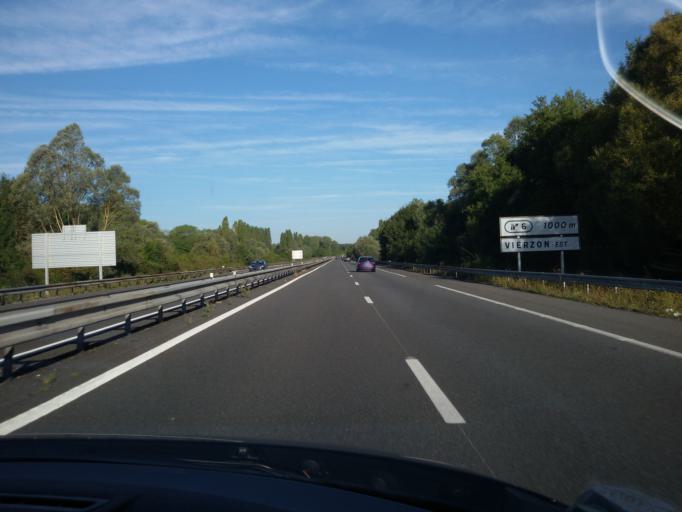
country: FR
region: Centre
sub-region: Departement du Cher
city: Foecy
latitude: 47.2013
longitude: 2.1351
